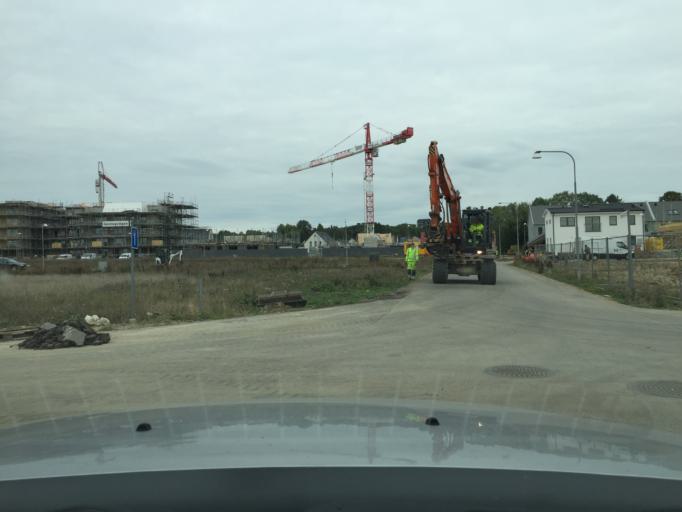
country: SE
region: Skane
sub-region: Lunds Kommun
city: Lund
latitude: 55.6898
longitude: 13.2303
